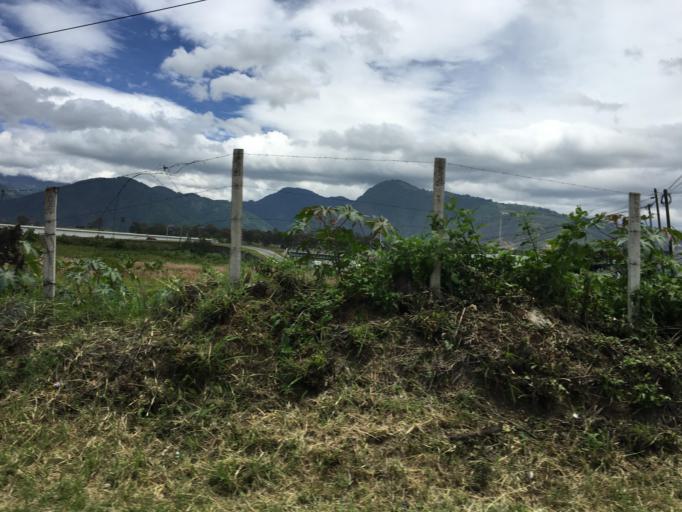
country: GT
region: Guatemala
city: Amatitlan
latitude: 14.5096
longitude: -90.6080
